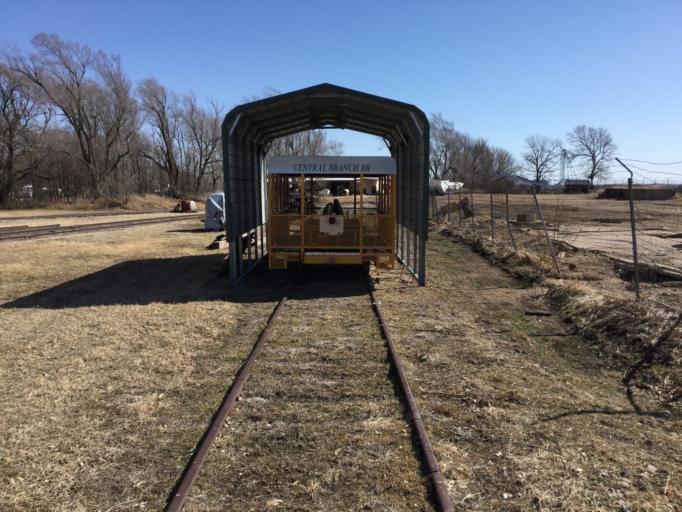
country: US
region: Kansas
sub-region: Marshall County
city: Blue Rapids
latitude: 39.6747
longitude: -96.6592
